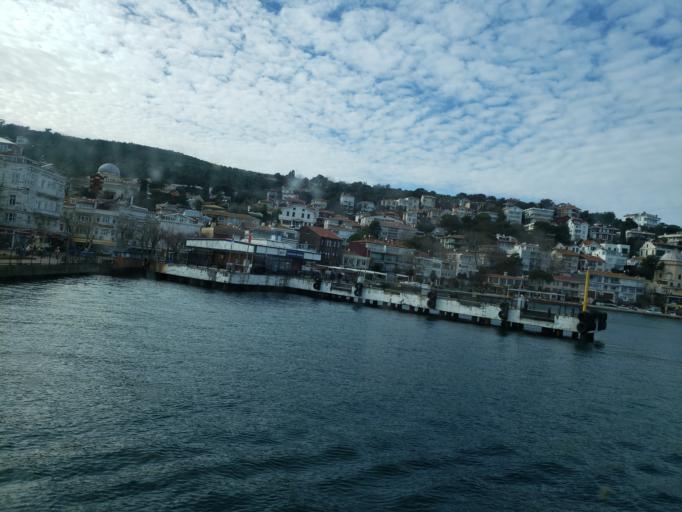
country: TR
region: Istanbul
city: Adalan
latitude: 40.8814
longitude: 29.0707
